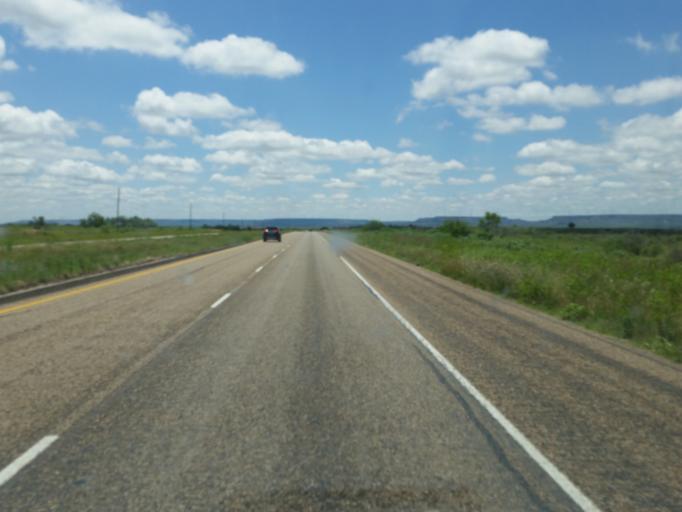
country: US
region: Texas
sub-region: Garza County
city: Post
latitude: 33.0857
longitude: -101.2425
